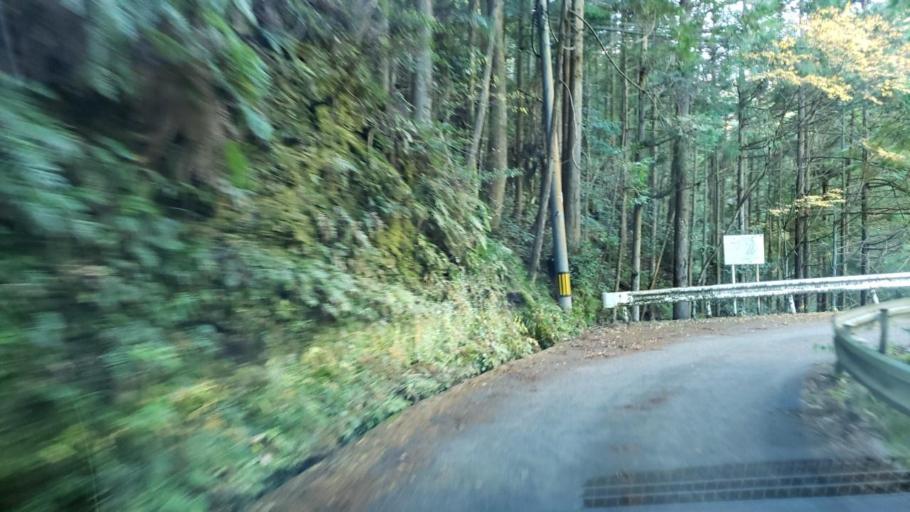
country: JP
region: Tokushima
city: Wakimachi
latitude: 33.9880
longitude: 134.0080
